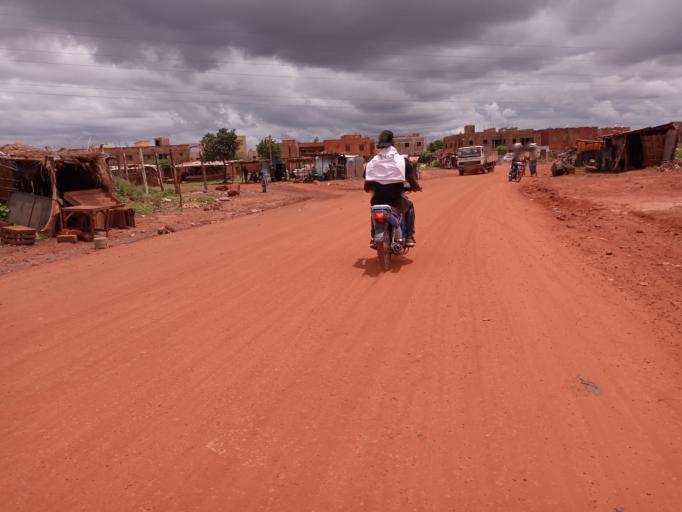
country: ML
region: Bamako
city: Bamako
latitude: 12.5473
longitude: -7.9952
